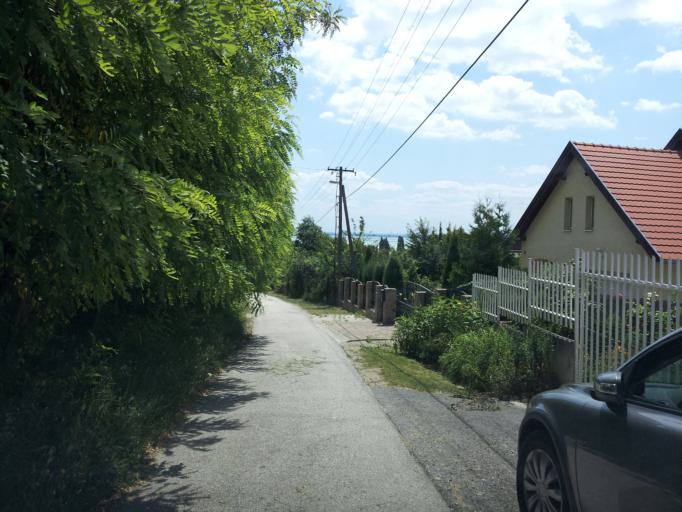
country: HU
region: Veszprem
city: Balatonkenese
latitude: 47.0375
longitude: 18.1165
